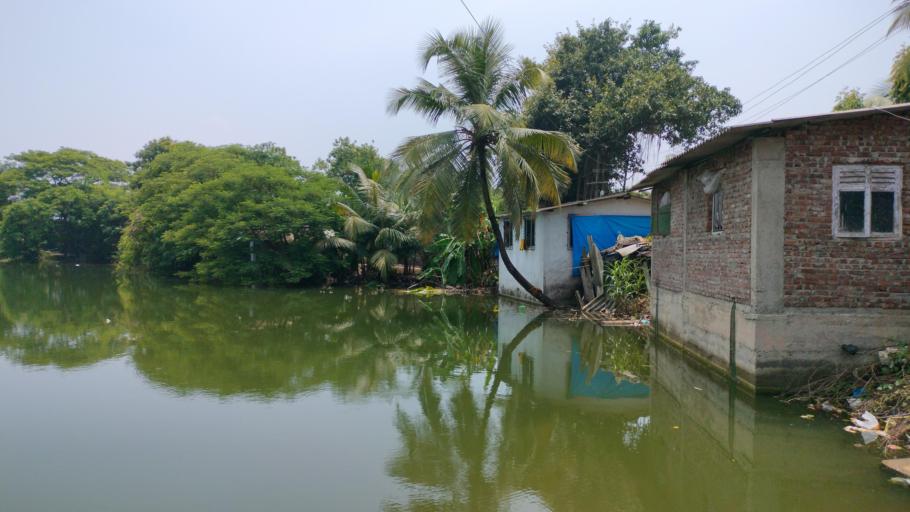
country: IN
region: Maharashtra
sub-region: Thane
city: Virar
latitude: 19.3838
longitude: 72.7761
